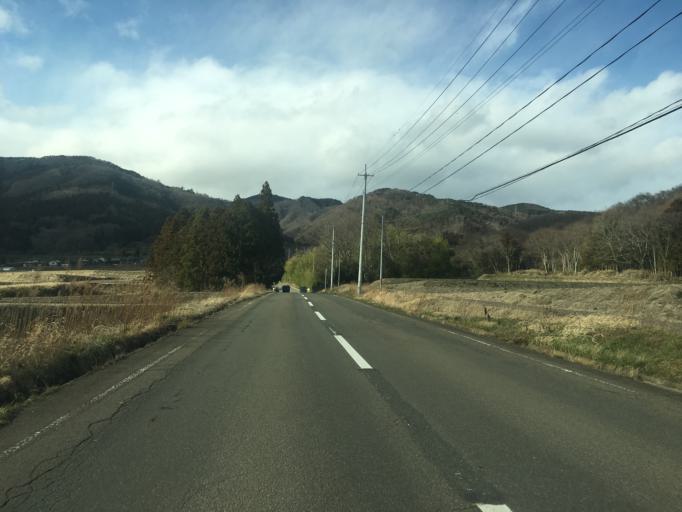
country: JP
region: Fukushima
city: Yanagawamachi-saiwaicho
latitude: 37.8983
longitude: 140.5797
